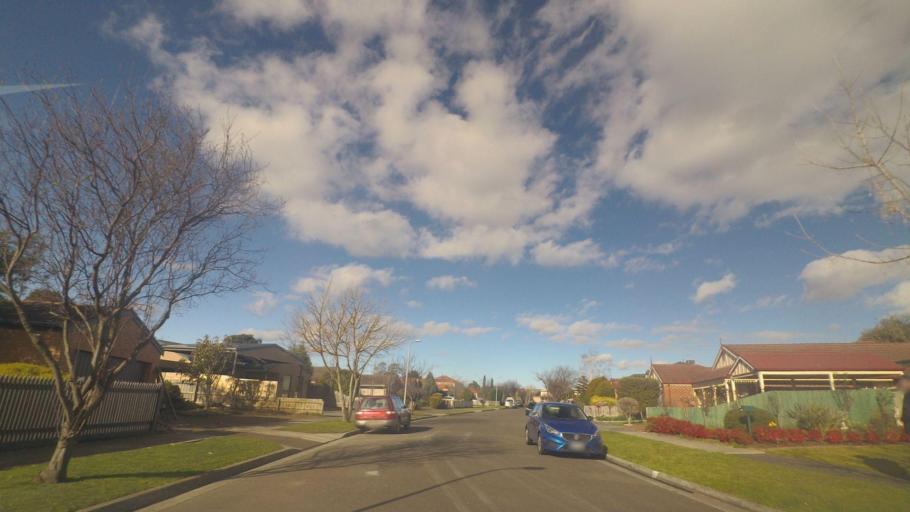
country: AU
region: Victoria
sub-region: Yarra Ranges
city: Lysterfield
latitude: -37.9138
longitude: 145.2787
